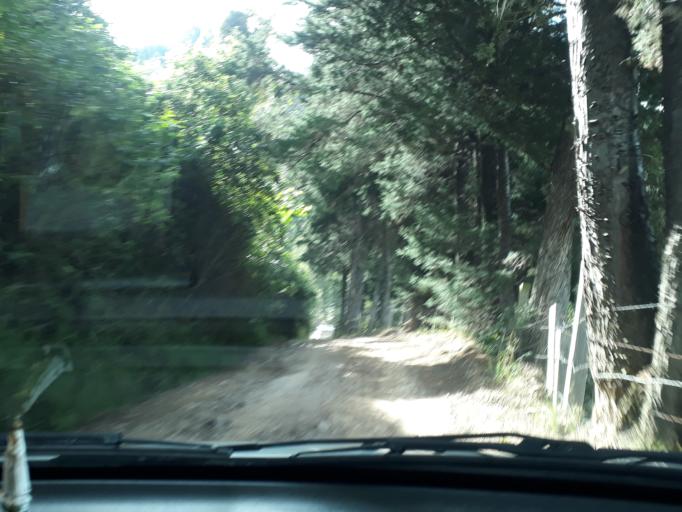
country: CO
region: Boyaca
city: Santa Rosa de Viterbo
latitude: 5.8580
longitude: -72.9704
